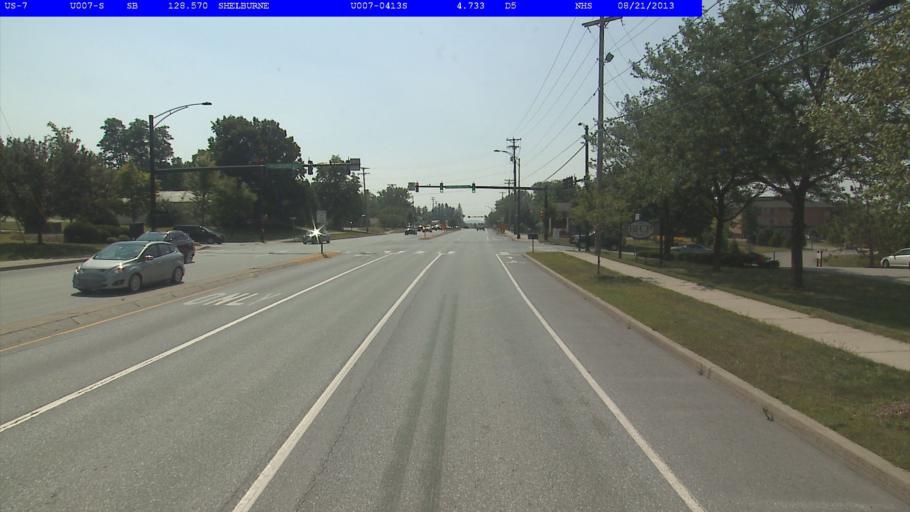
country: US
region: Vermont
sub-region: Chittenden County
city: Burlington
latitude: 44.4196
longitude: -73.2124
